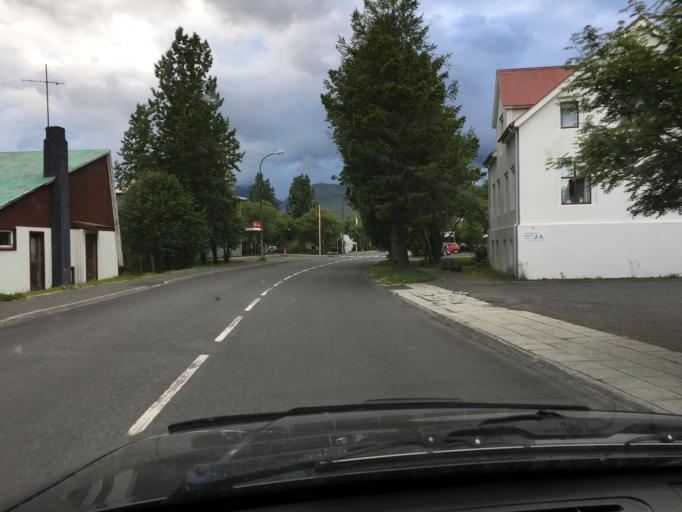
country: IS
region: East
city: Reydarfjoerdur
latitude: 65.0329
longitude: -14.2195
